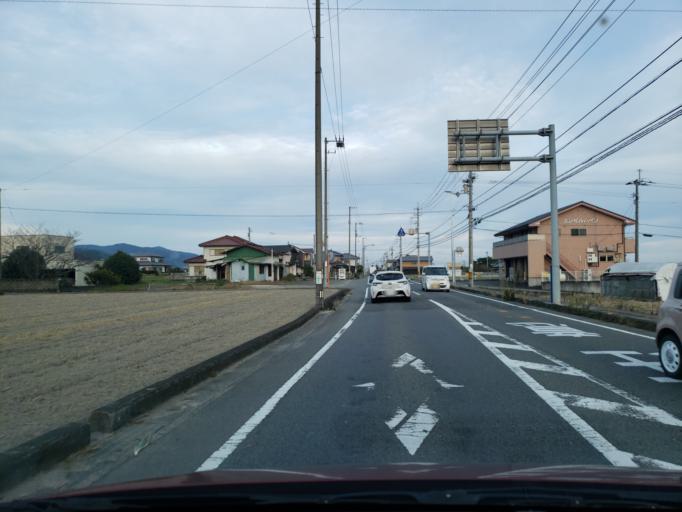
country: JP
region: Tokushima
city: Kamojimacho-jogejima
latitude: 34.0876
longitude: 134.2940
